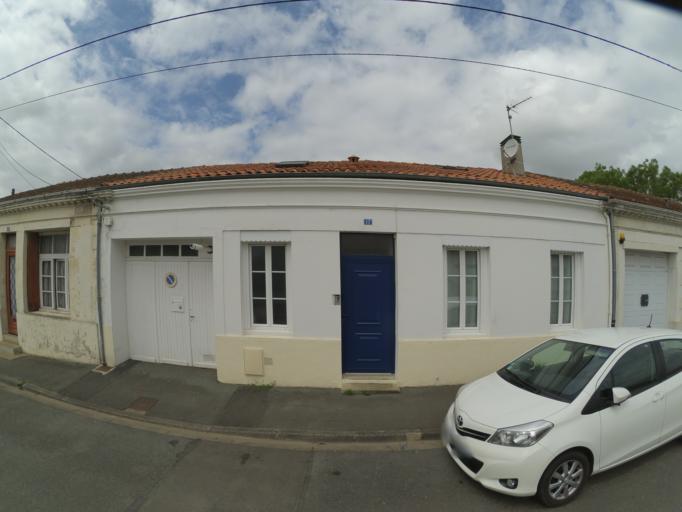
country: FR
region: Poitou-Charentes
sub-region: Departement de la Charente-Maritime
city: Rochefort
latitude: 45.9492
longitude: -0.9685
